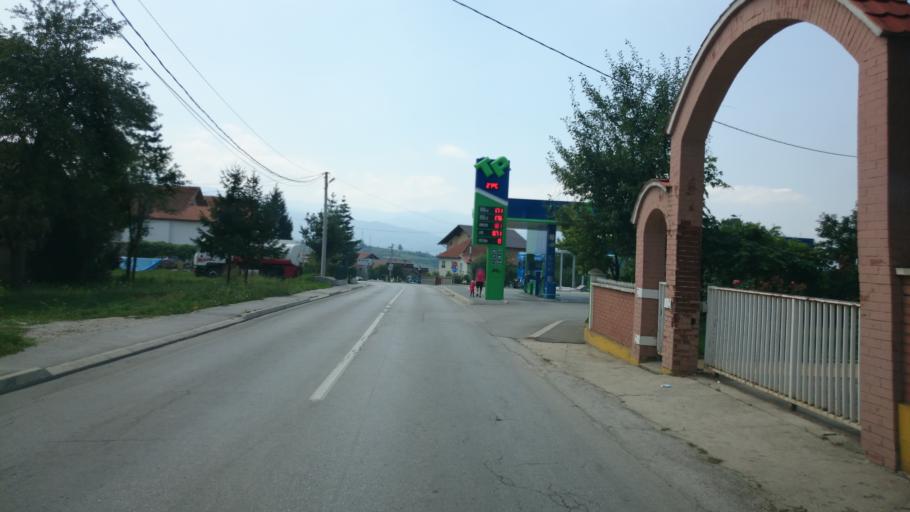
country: BA
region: Federation of Bosnia and Herzegovina
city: Lokvine
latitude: 44.1692
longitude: 17.8358
